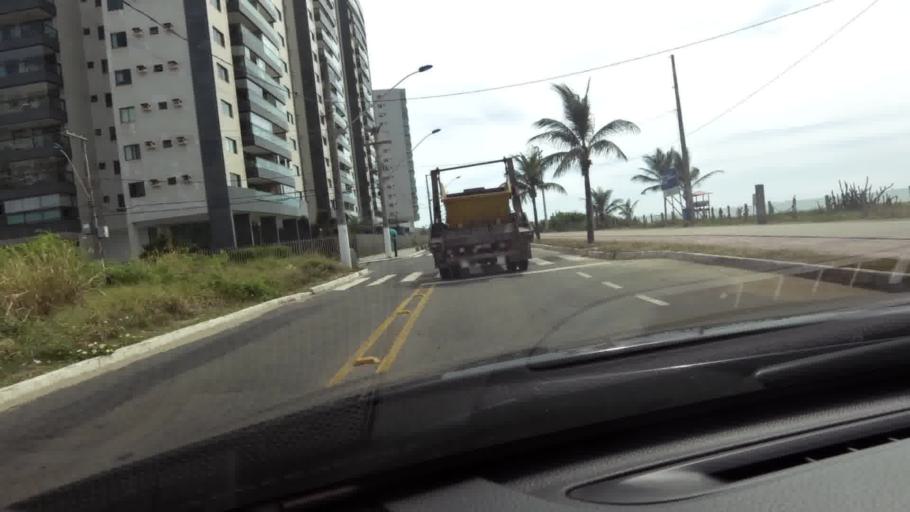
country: BR
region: Espirito Santo
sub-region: Vila Velha
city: Vila Velha
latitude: -20.3791
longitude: -40.3073
